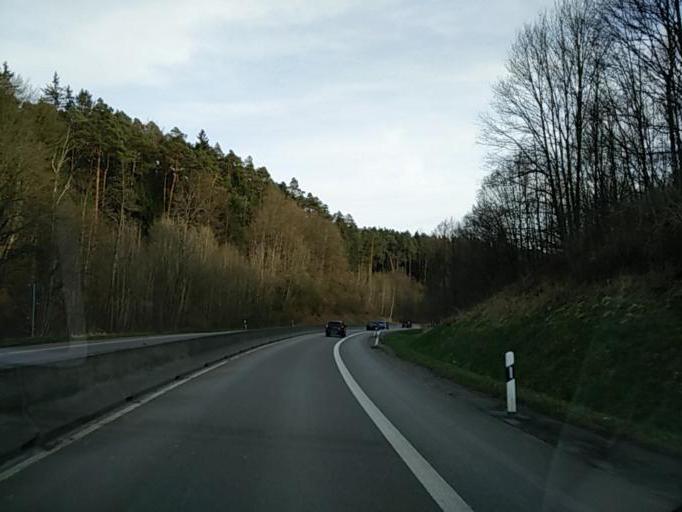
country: DE
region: Baden-Wuerttemberg
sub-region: Tuebingen Region
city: Dettenhausen
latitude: 48.5791
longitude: 9.0680
